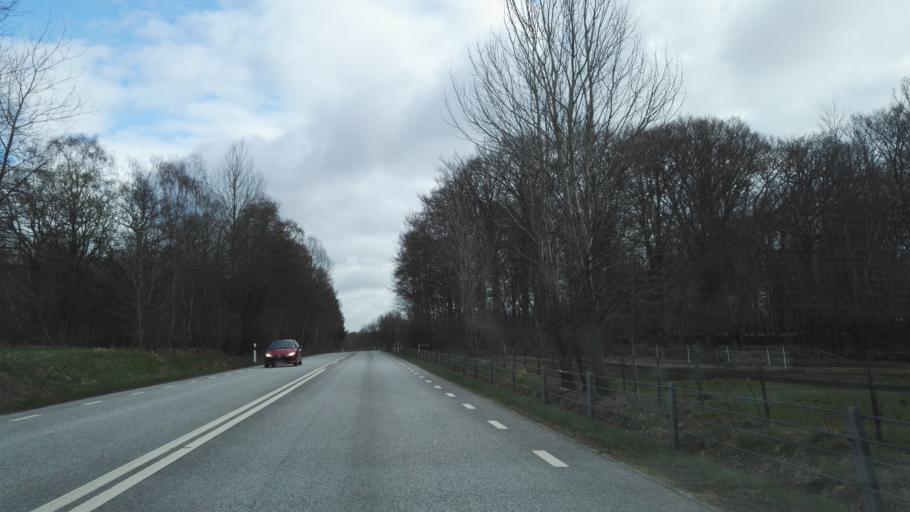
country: SE
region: Skane
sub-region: Hoors Kommun
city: Satofta
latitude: 55.9242
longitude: 13.5841
